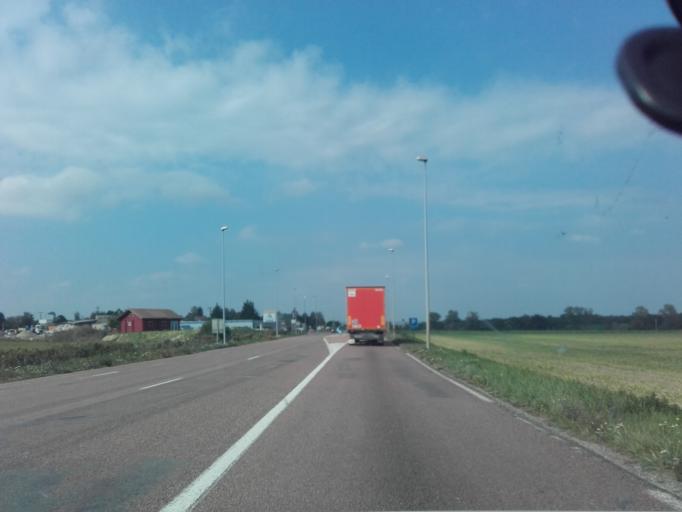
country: FR
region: Bourgogne
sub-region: Departement de Saone-et-Loire
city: Champforgeuil
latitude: 46.8406
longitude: 4.8155
